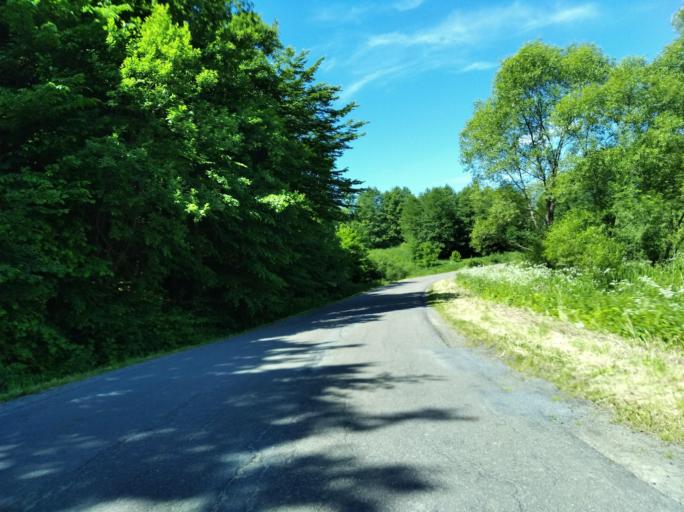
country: PL
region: Subcarpathian Voivodeship
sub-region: Powiat krosnienski
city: Chorkowka
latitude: 49.6355
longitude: 21.5990
